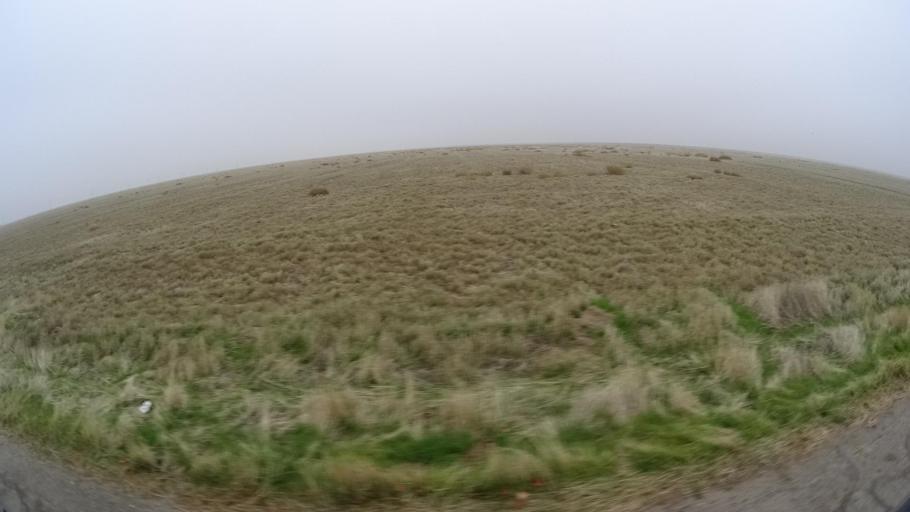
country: US
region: California
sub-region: Tulare County
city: Alpaugh
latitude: 35.7857
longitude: -119.4011
